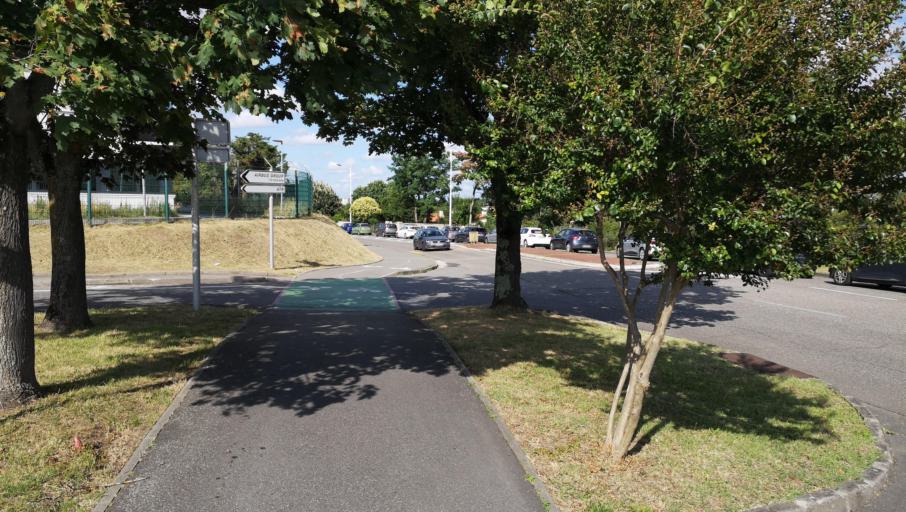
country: FR
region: Midi-Pyrenees
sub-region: Departement de la Haute-Garonne
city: Blagnac
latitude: 43.6209
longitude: 1.3902
